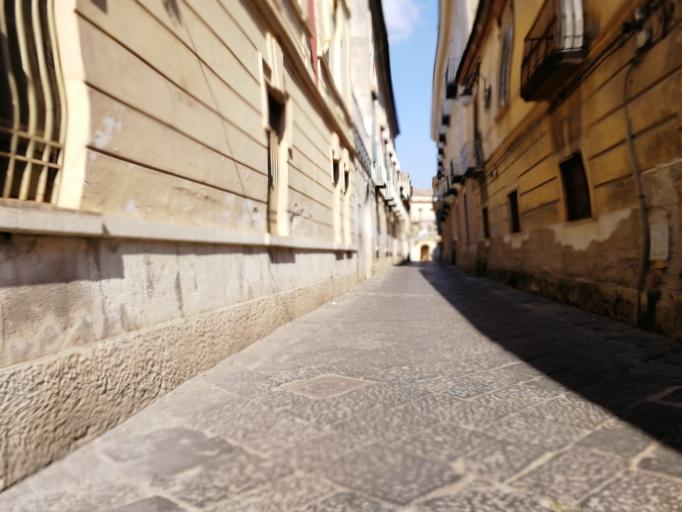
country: IT
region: Campania
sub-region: Provincia di Caserta
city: Santa Maria Capua Vetere
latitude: 41.0795
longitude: 14.2570
